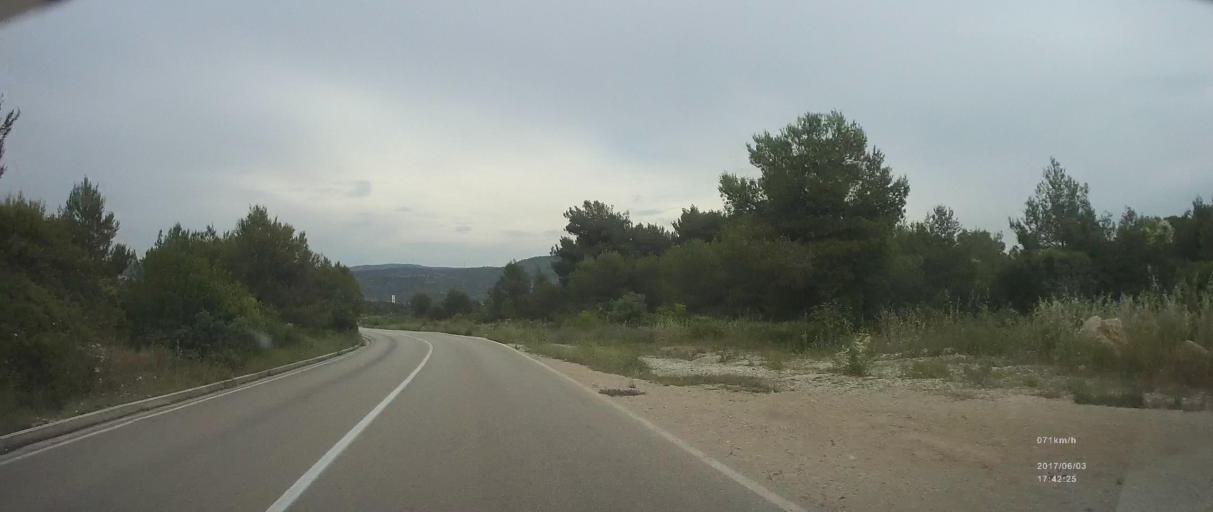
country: HR
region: Sibensko-Kniniska
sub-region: Grad Sibenik
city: Sibenik
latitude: 43.7068
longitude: 15.8963
